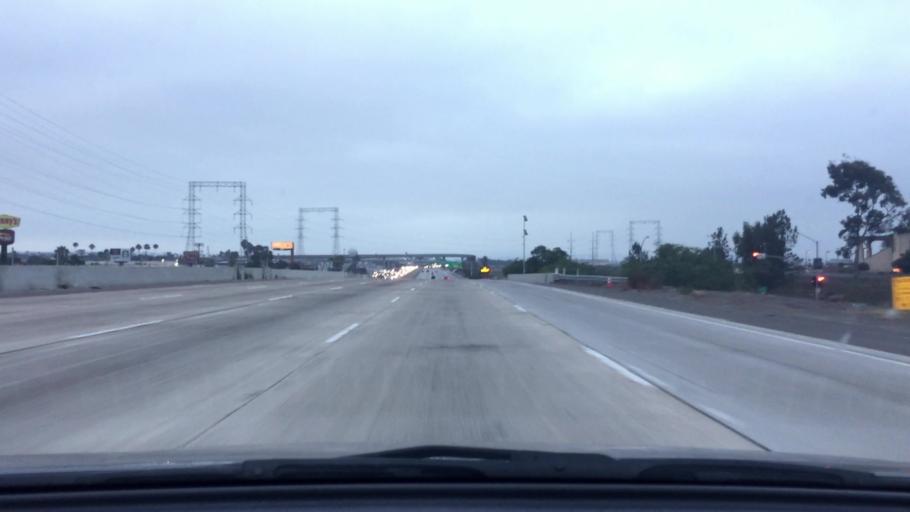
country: US
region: California
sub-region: San Diego County
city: National City
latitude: 32.6609
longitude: -117.1086
